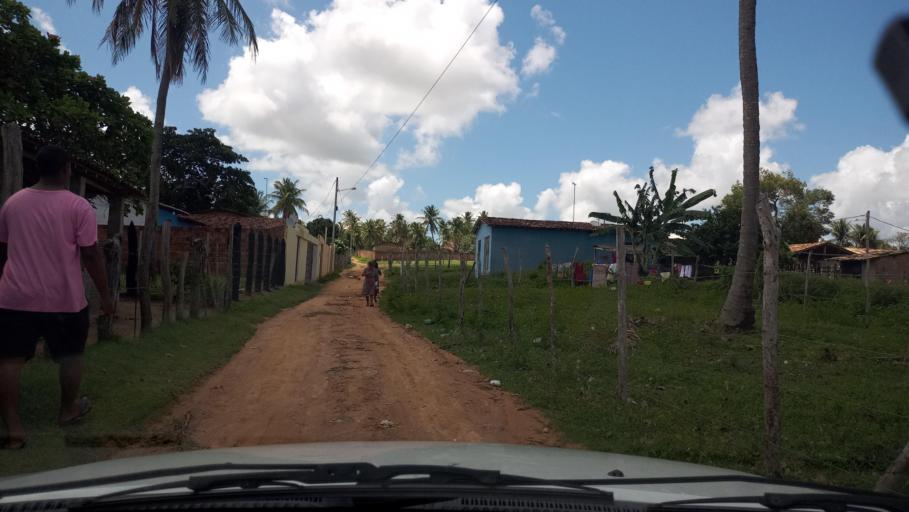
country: BR
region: Rio Grande do Norte
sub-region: Goianinha
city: Goianinha
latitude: -6.2969
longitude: -35.2231
